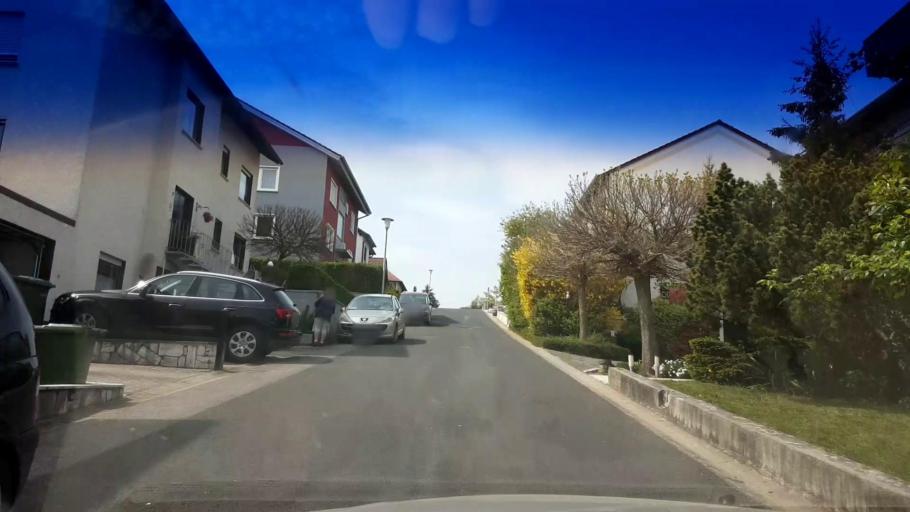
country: DE
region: Bavaria
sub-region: Upper Franconia
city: Baunach
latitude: 49.9875
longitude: 10.8457
